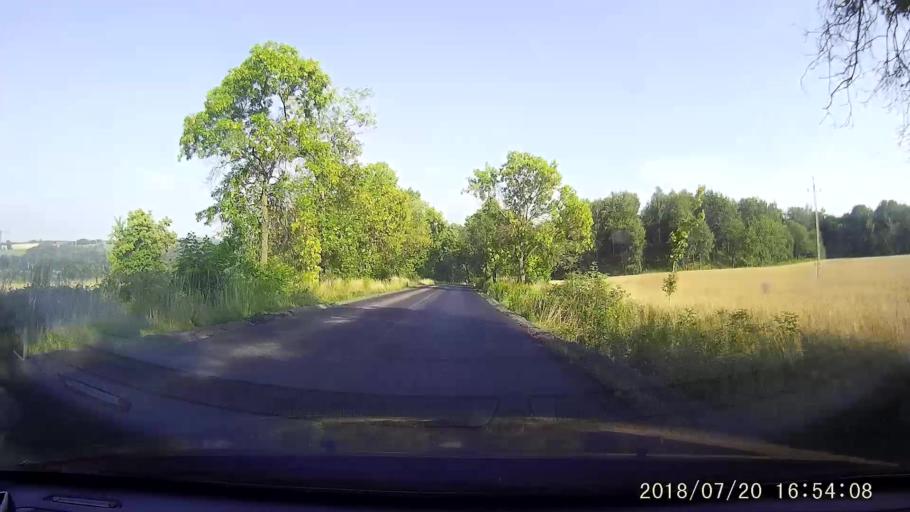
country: PL
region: Lower Silesian Voivodeship
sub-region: Powiat lubanski
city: Lesna
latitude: 51.0336
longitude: 15.2479
